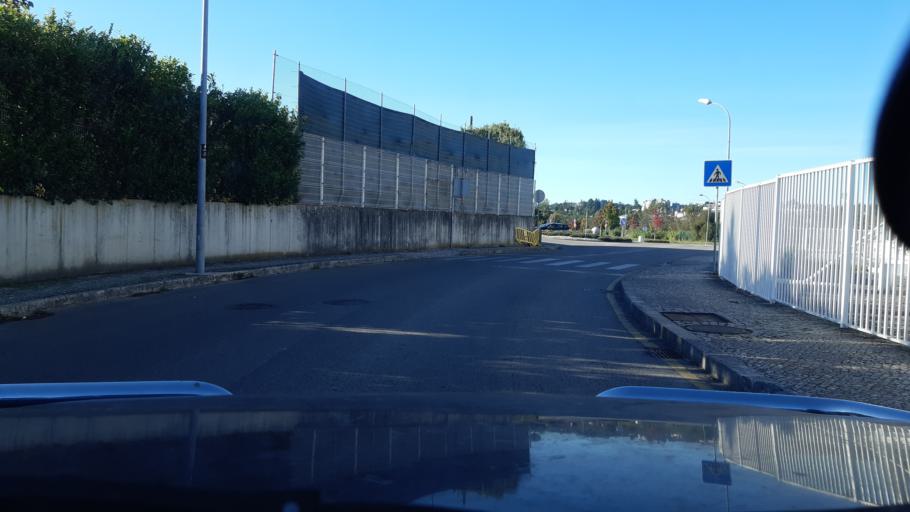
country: PT
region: Aveiro
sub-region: Agueda
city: Agueda
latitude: 40.5618
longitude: -8.4426
